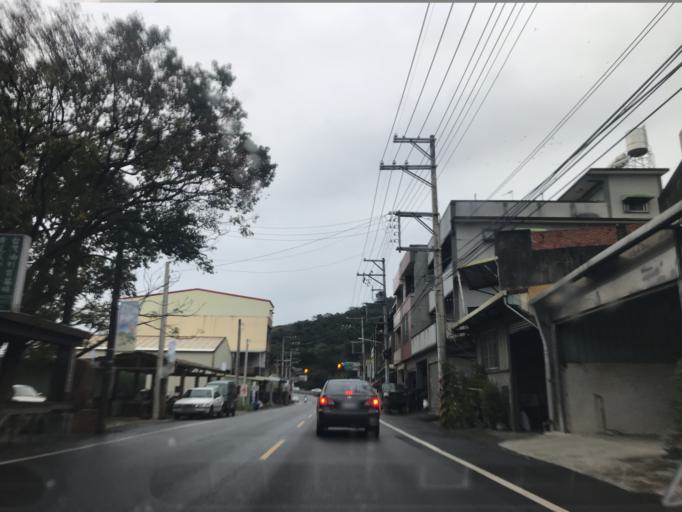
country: TW
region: Taiwan
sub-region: Hsinchu
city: Zhubei
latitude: 24.8392
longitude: 121.1015
